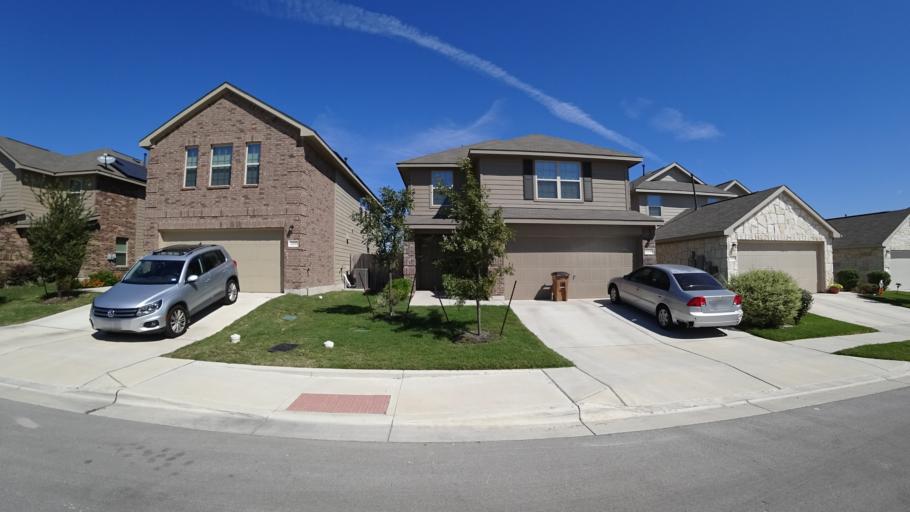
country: US
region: Texas
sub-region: Travis County
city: Austin
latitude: 30.2023
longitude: -97.6960
